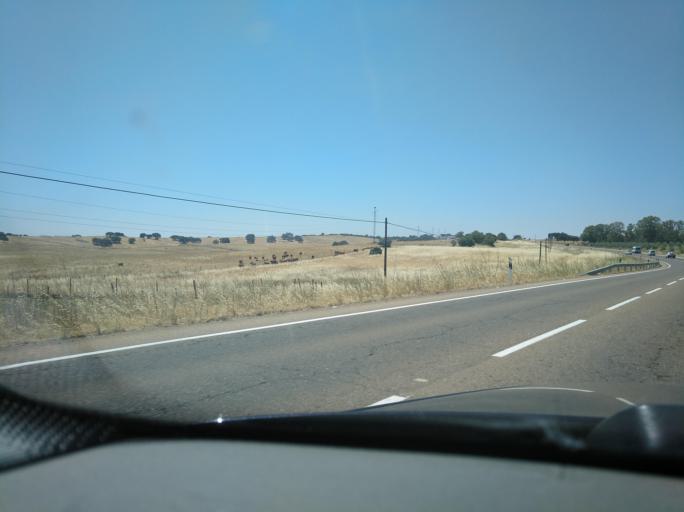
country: ES
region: Extremadura
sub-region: Provincia de Badajoz
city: Olivenza
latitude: 38.7244
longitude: -7.0793
